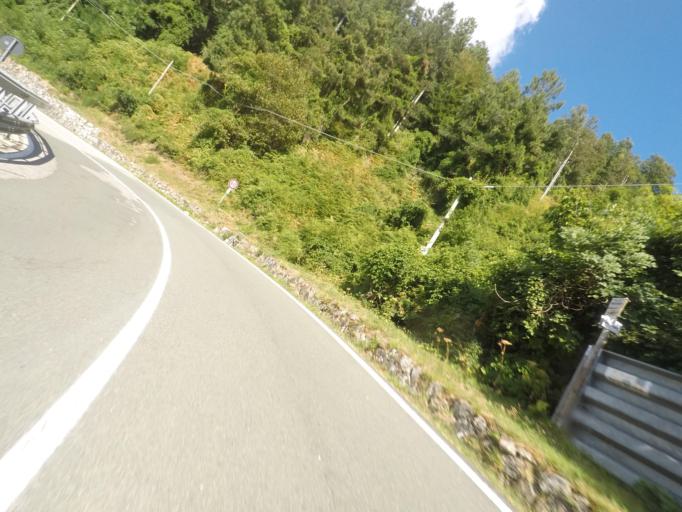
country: IT
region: Tuscany
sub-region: Provincia di Massa-Carrara
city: Comano
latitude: 44.2652
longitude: 10.1789
